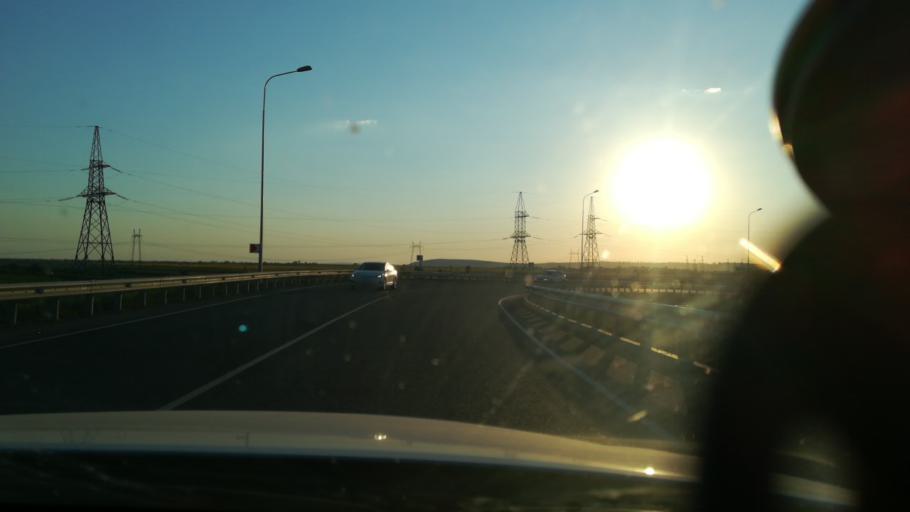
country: RU
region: Krasnodarskiy
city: Dzhiginka
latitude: 45.1368
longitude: 37.3164
